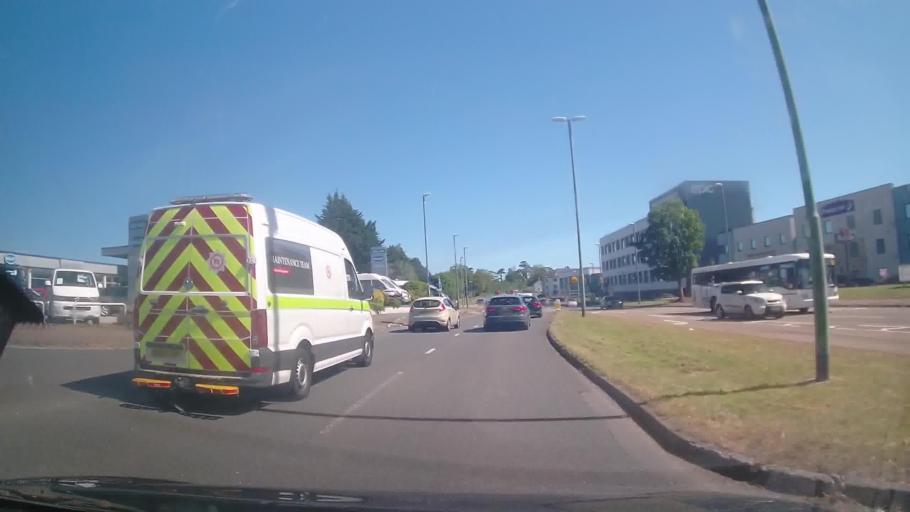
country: GB
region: England
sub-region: Borough of Torbay
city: Paignton
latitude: 50.4144
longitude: -3.5789
